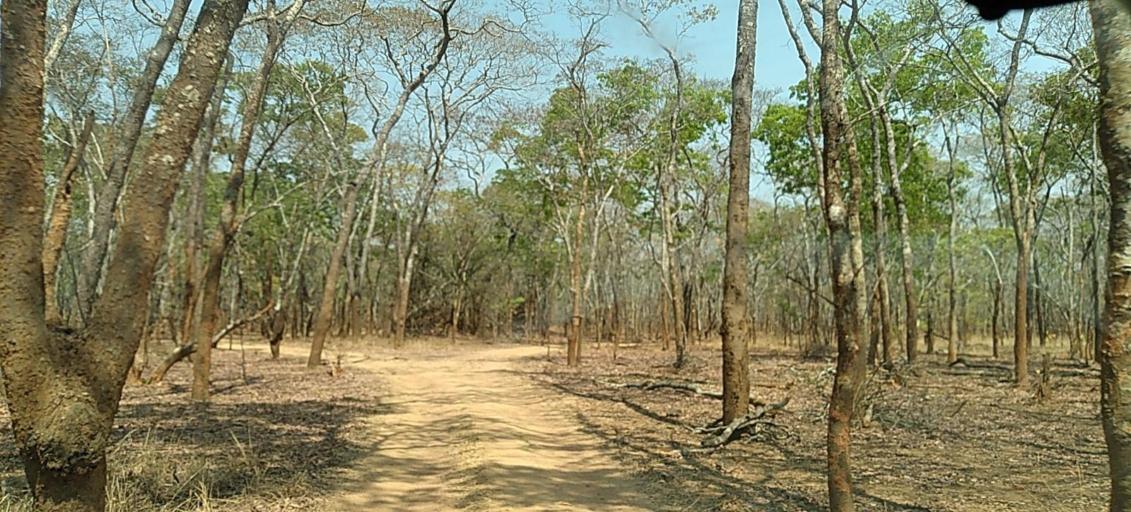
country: ZM
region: North-Western
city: Kasempa
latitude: -13.3930
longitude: 25.6036
